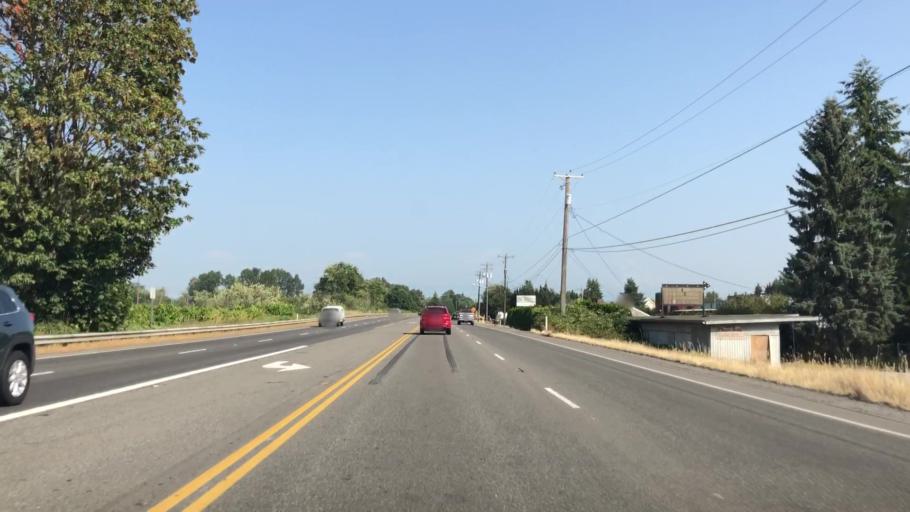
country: US
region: Washington
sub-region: Pierce County
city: Fife
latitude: 47.2241
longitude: -122.3621
